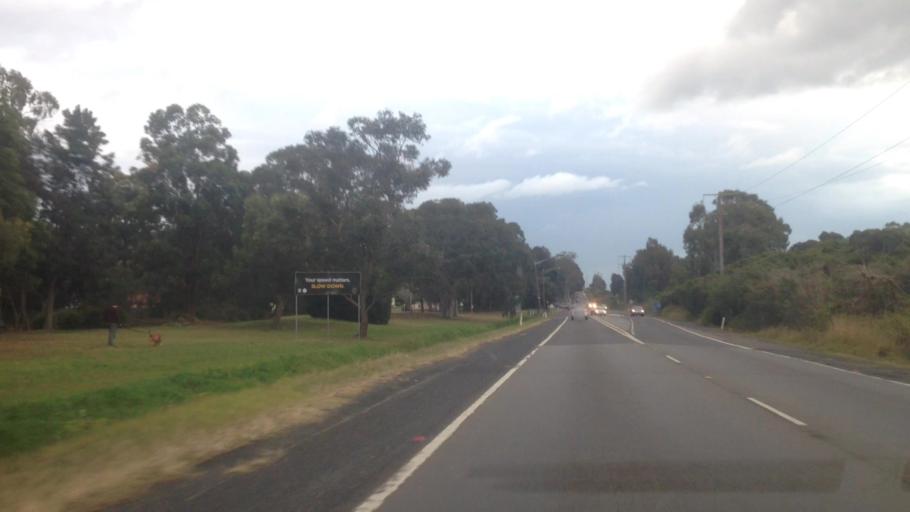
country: AU
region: New South Wales
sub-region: Wyong Shire
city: Chittaway Bay
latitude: -33.2780
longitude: 151.4279
